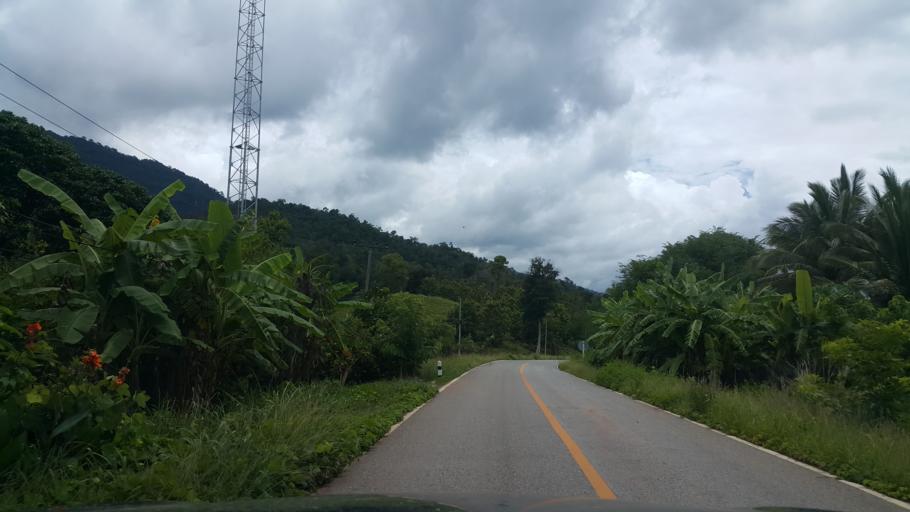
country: TH
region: Phitsanulok
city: Chat Trakan
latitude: 17.3888
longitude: 100.7577
